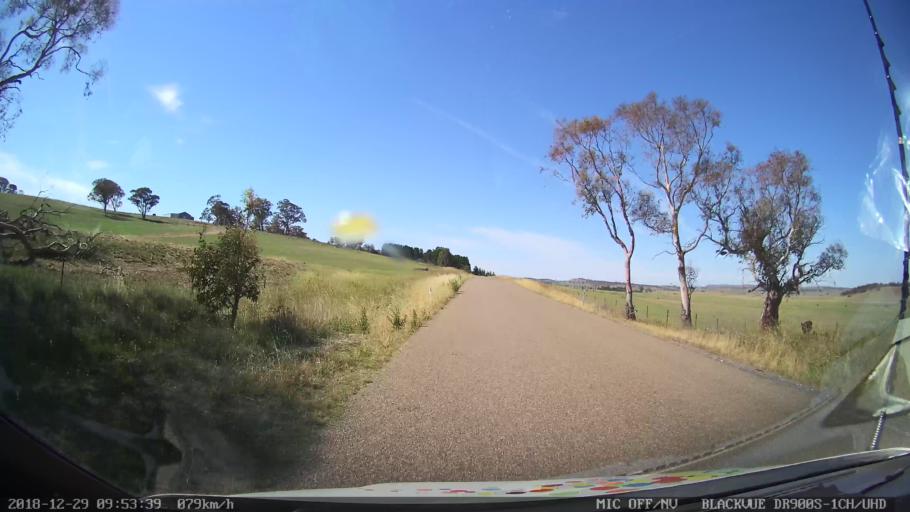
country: AU
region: New South Wales
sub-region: Goulburn Mulwaree
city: Goulburn
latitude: -34.7543
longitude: 149.4689
